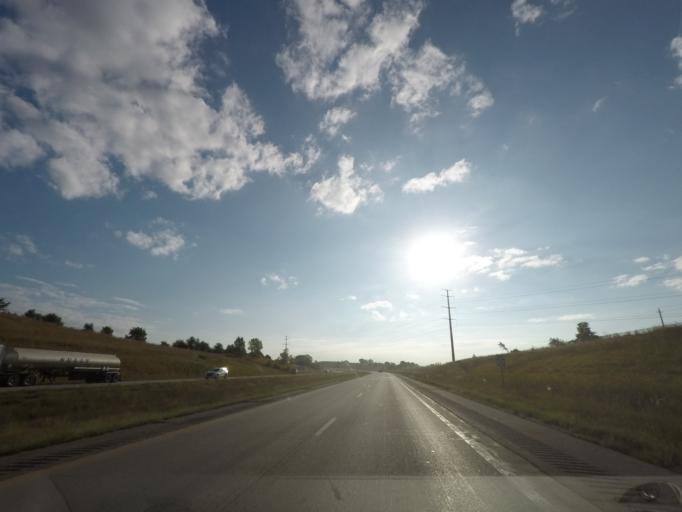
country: US
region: Iowa
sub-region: Warren County
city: Norwalk
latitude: 41.4981
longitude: -93.6132
